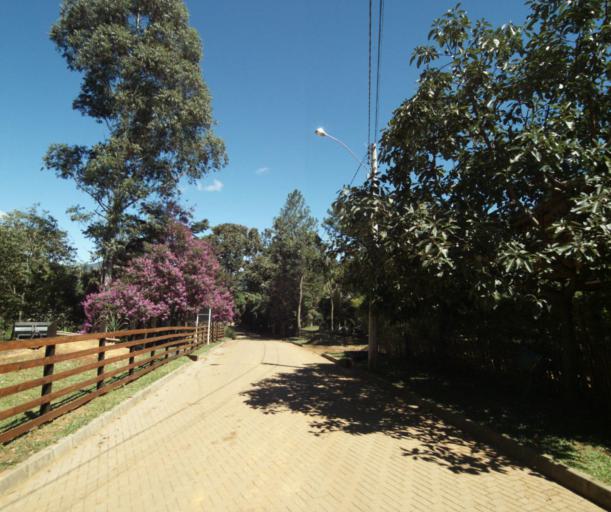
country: BR
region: Minas Gerais
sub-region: Espera Feliz
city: Espera Feliz
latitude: -20.5507
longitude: -41.8106
